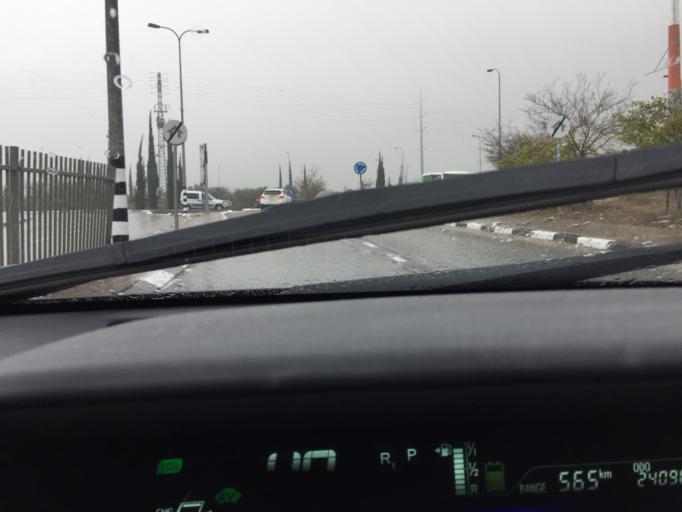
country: PS
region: West Bank
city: Kifil Haris
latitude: 32.1083
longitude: 35.1655
